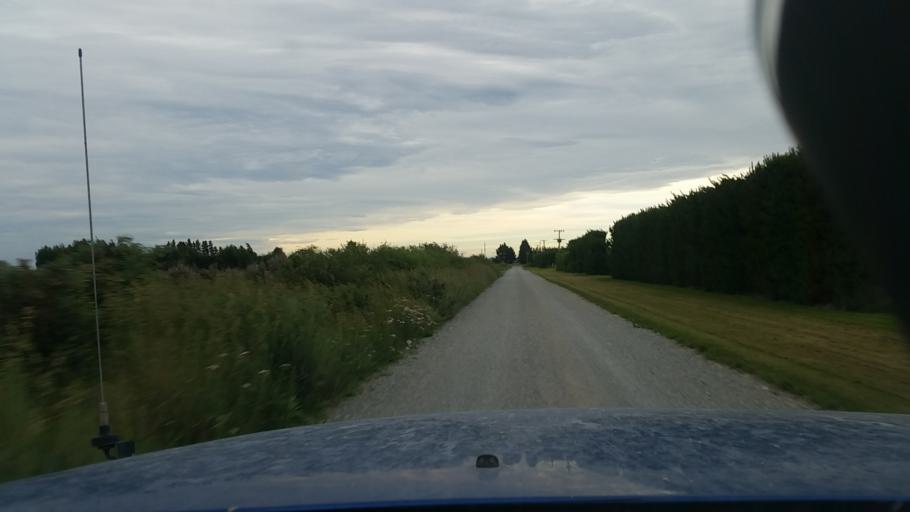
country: NZ
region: Canterbury
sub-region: Ashburton District
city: Tinwald
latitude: -43.9510
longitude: 171.6621
